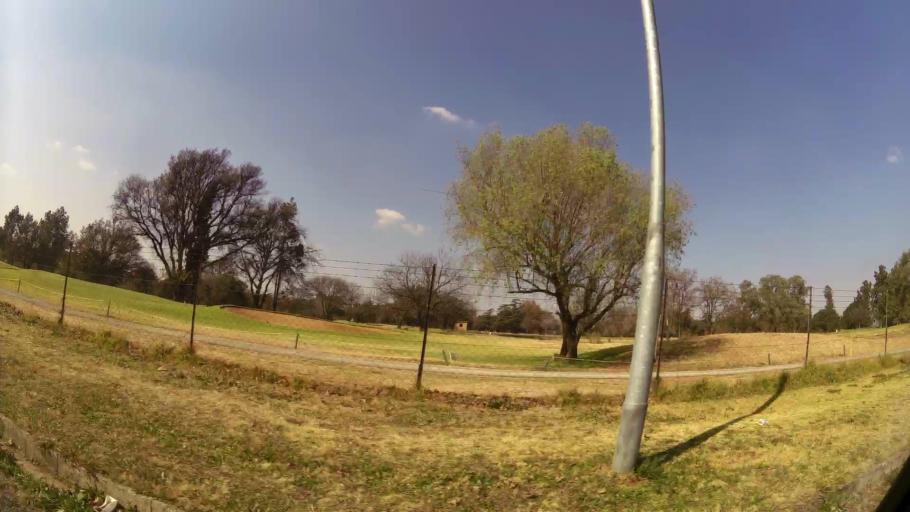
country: ZA
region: Gauteng
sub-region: Ekurhuleni Metropolitan Municipality
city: Benoni
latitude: -26.1849
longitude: 28.2917
